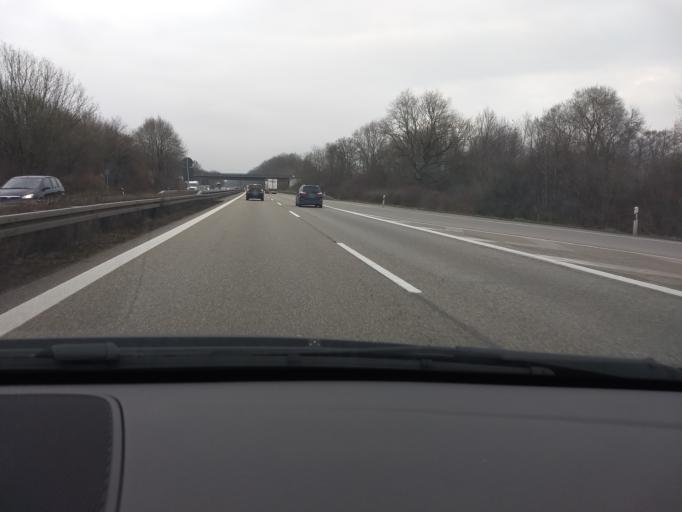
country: DE
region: Baden-Wuerttemberg
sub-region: Freiburg Region
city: Teningen
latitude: 48.1173
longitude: 7.7870
